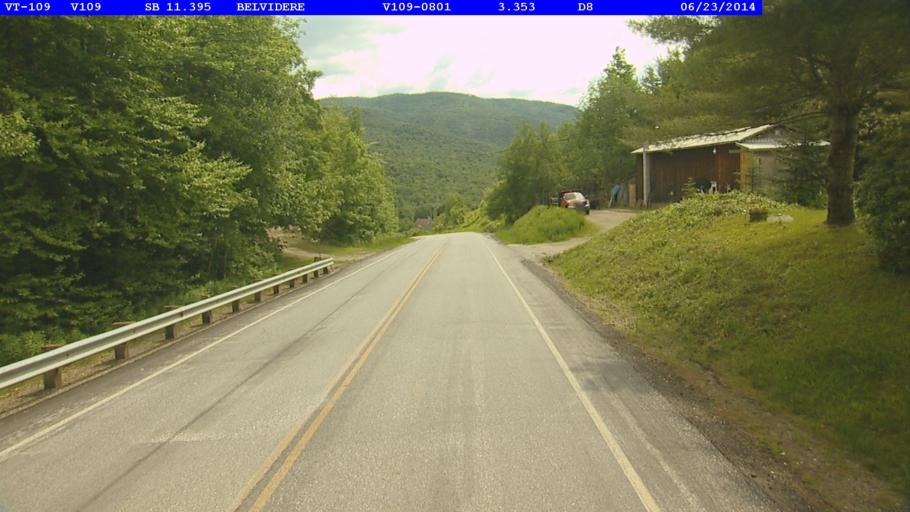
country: US
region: Vermont
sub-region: Lamoille County
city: Johnson
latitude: 44.7542
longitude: -72.6846
